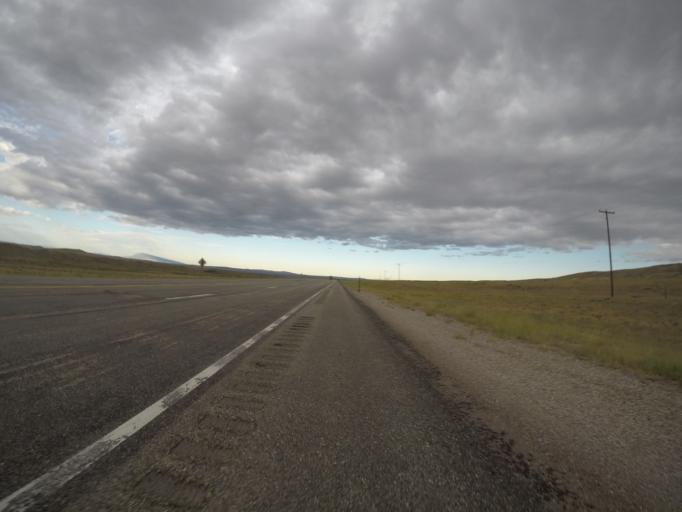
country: US
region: Wyoming
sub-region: Albany County
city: Laramie
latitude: 41.8651
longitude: -106.0982
